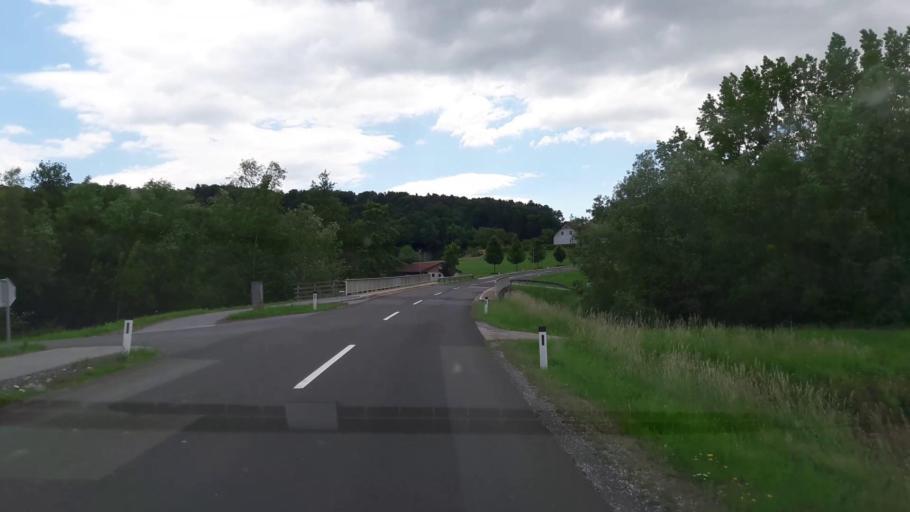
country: AT
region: Styria
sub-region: Politischer Bezirk Hartberg-Fuerstenfeld
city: Soechau
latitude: 47.0630
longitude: 16.0085
